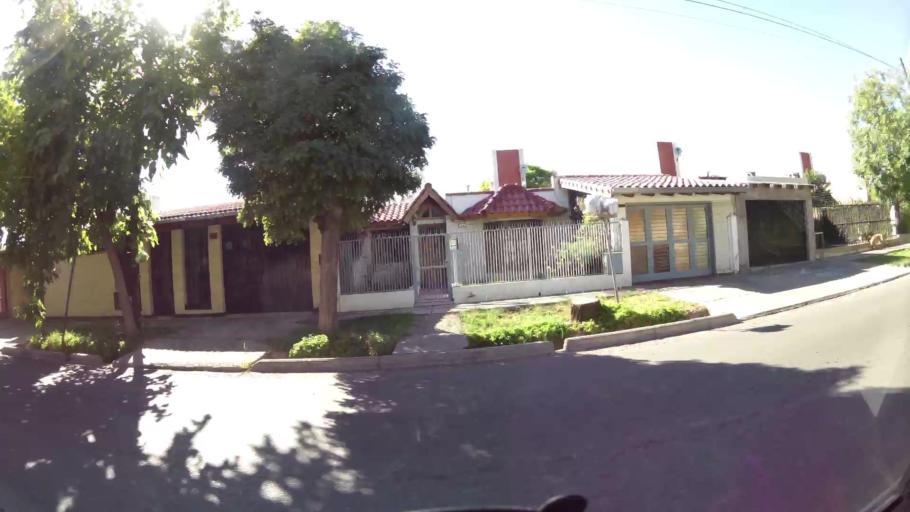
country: AR
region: Mendoza
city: Mendoza
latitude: -32.8761
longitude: -68.8727
